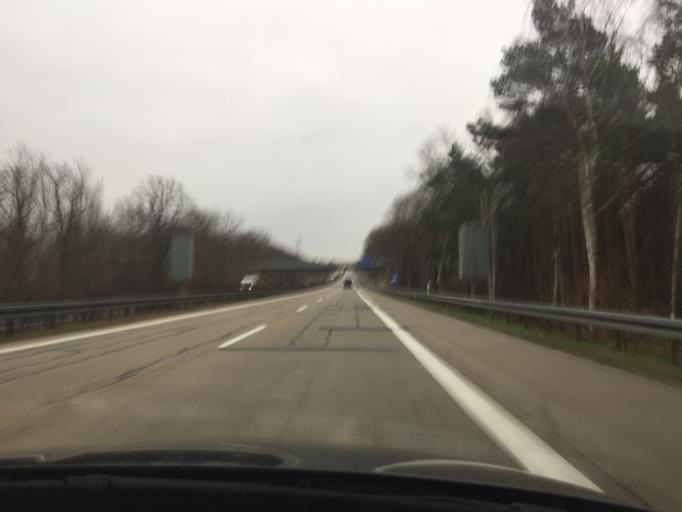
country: DE
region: Brandenburg
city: Lubbenau
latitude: 51.8340
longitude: 13.9728
